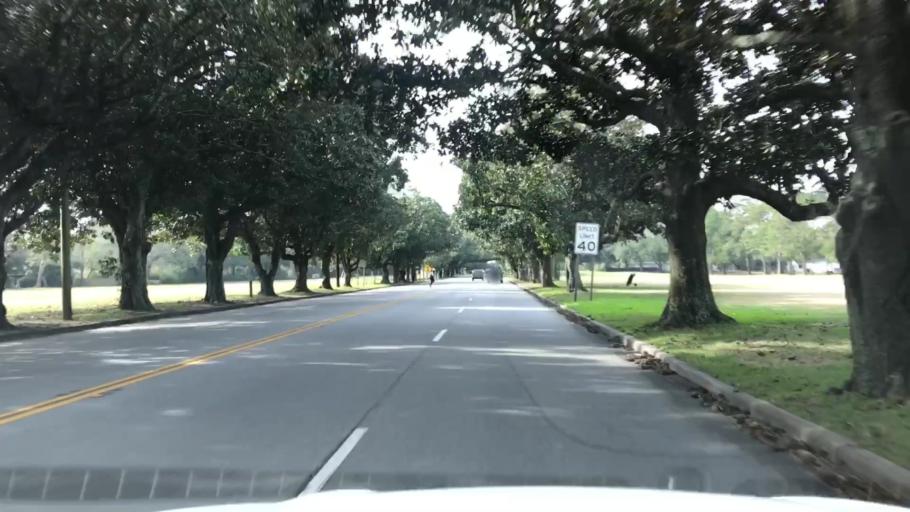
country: US
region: South Carolina
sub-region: Charleston County
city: Charleston
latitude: 32.7579
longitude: -79.9949
